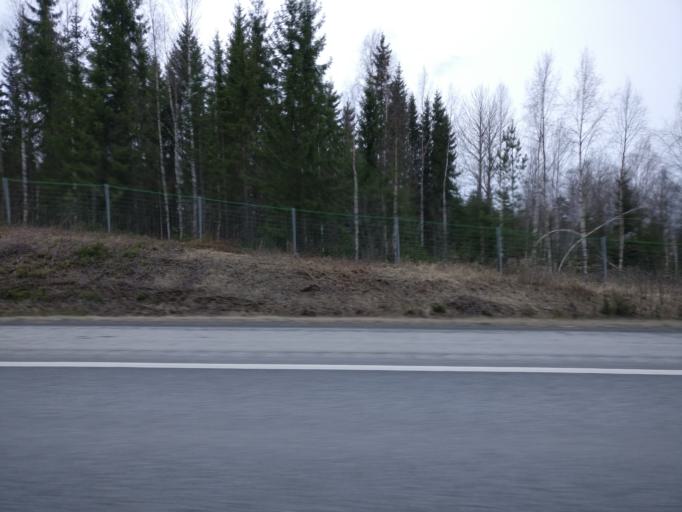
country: FI
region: Pirkanmaa
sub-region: Etelae-Pirkanmaa
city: Viiala
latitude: 61.2665
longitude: 23.8256
